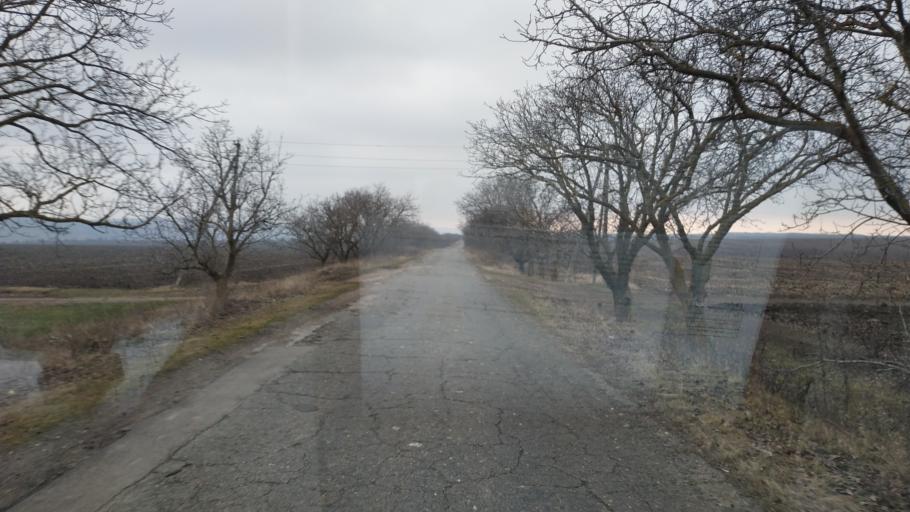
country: MD
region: Hincesti
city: Dancu
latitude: 46.8859
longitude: 28.3003
